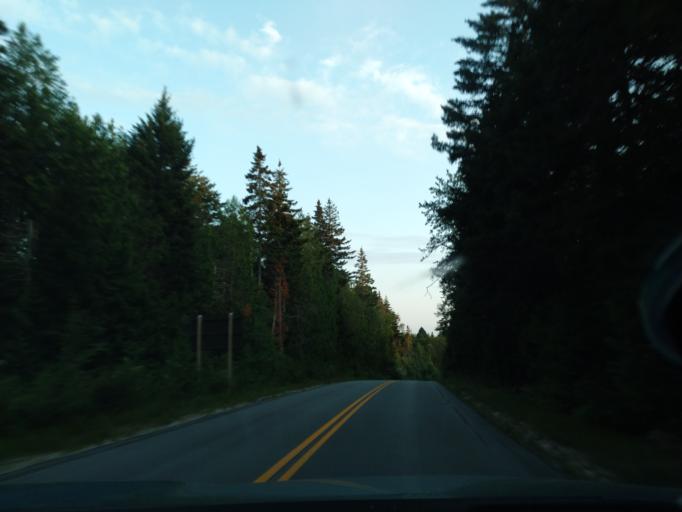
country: US
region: Maine
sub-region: Hancock County
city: Gouldsboro
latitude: 44.3793
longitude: -68.0685
